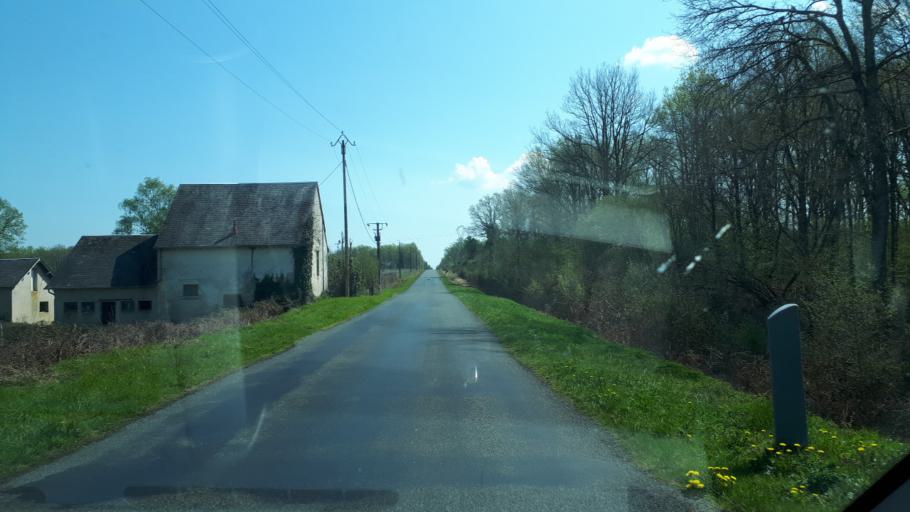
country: FR
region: Centre
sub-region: Departement du Cher
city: Neuvy-sur-Barangeon
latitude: 47.3203
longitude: 2.1912
